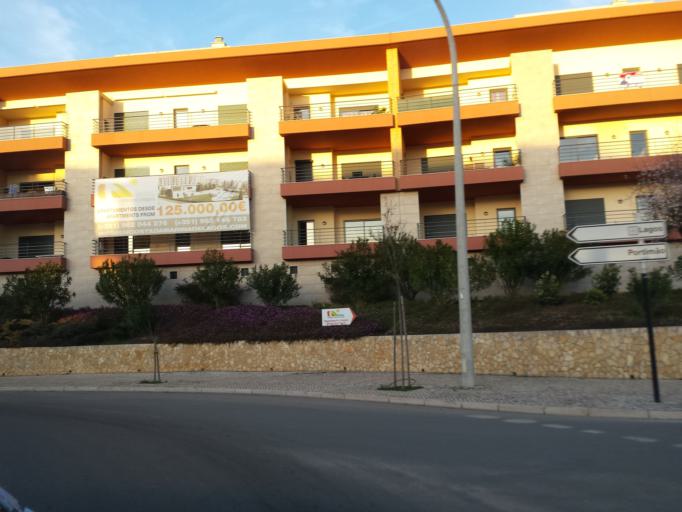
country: PT
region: Faro
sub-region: Lagos
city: Lagos
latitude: 37.1114
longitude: -8.6717
